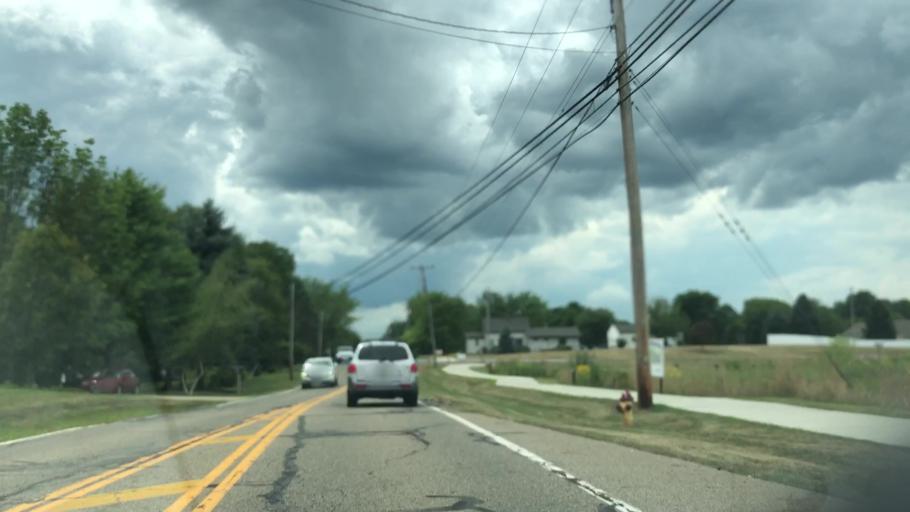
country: US
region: Ohio
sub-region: Summit County
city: Green
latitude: 40.9478
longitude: -81.4740
